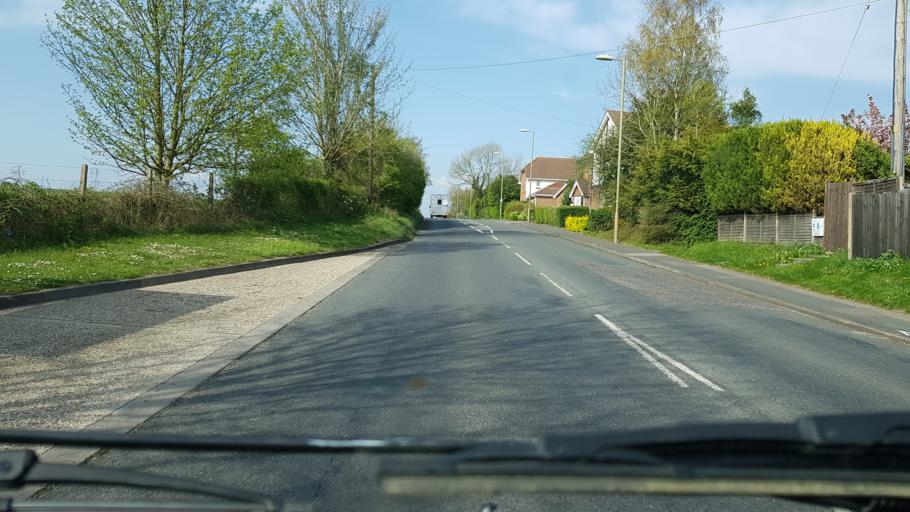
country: GB
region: England
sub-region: Hampshire
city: Basingstoke
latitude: 51.2659
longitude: -1.1326
